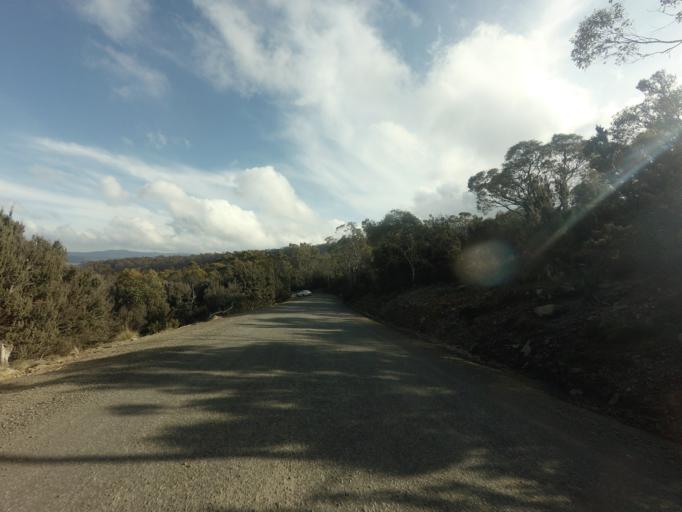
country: AU
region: Tasmania
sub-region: Meander Valley
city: Deloraine
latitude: -41.7758
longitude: 146.7095
